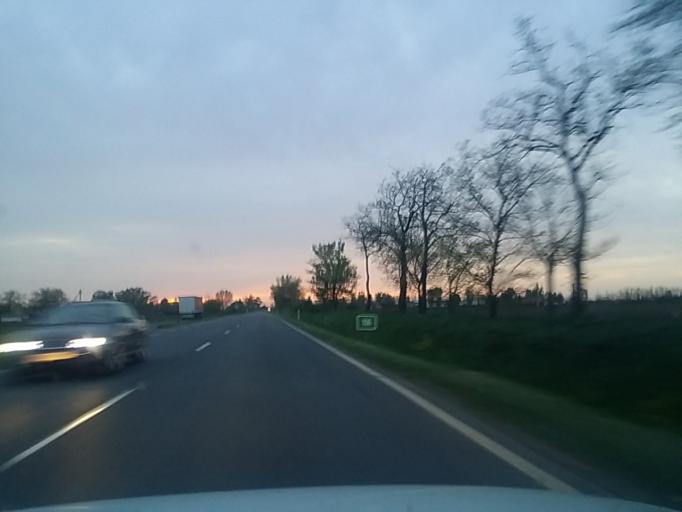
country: HU
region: Bekes
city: Kondoros
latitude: 46.7315
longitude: 20.9040
